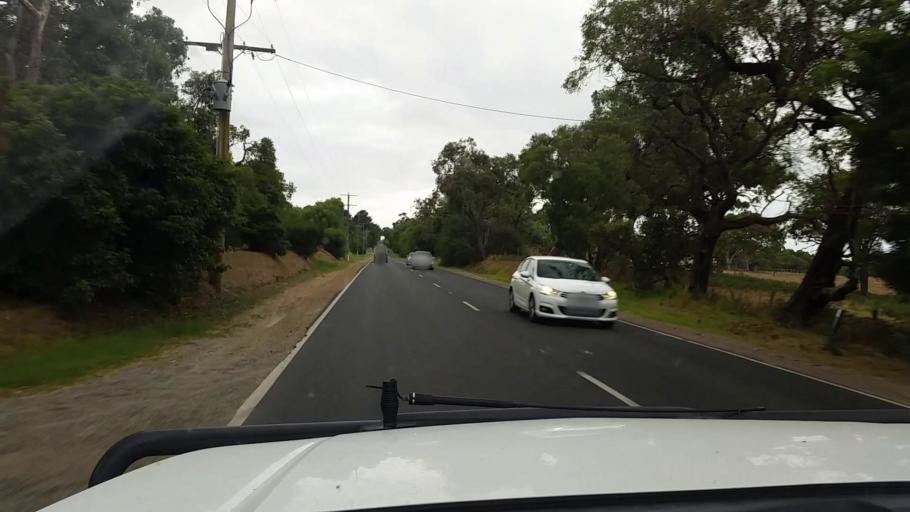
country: AU
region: Victoria
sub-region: Mornington Peninsula
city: Langwarrin South
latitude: -38.1992
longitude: 145.1867
